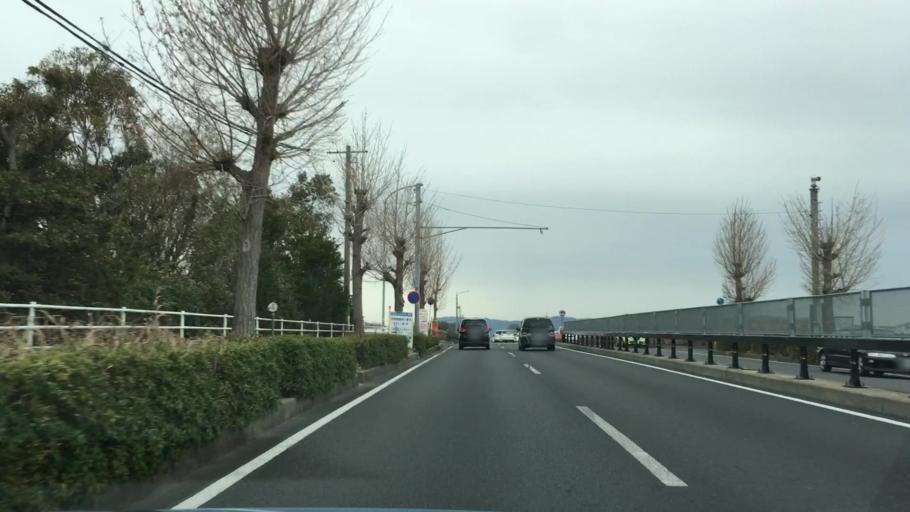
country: JP
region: Aichi
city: Kozakai-cho
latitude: 34.7919
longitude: 137.3718
